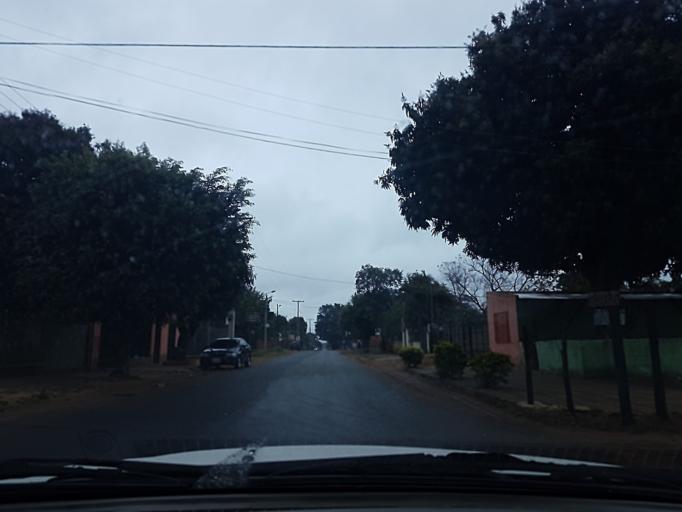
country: PY
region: Central
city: San Lorenzo
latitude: -25.2746
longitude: -57.4676
